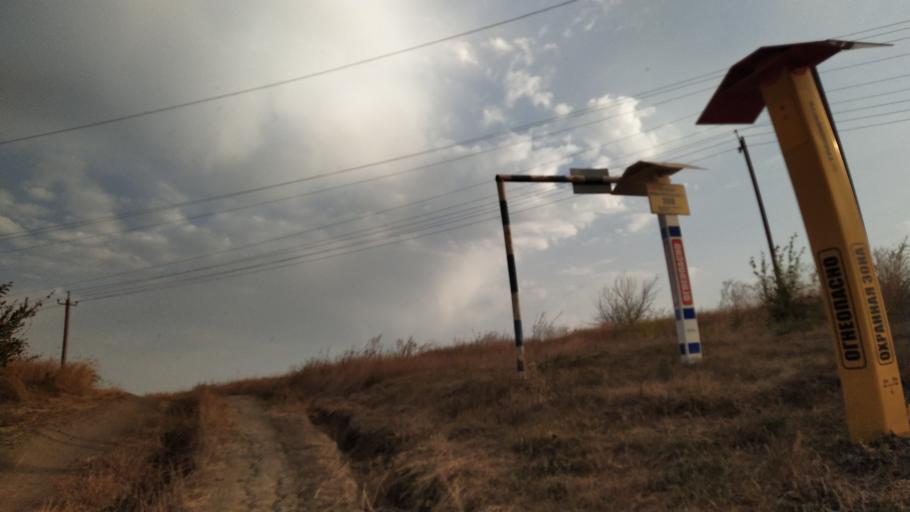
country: RU
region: Rostov
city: Kuleshovka
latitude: 47.1091
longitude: 39.6139
